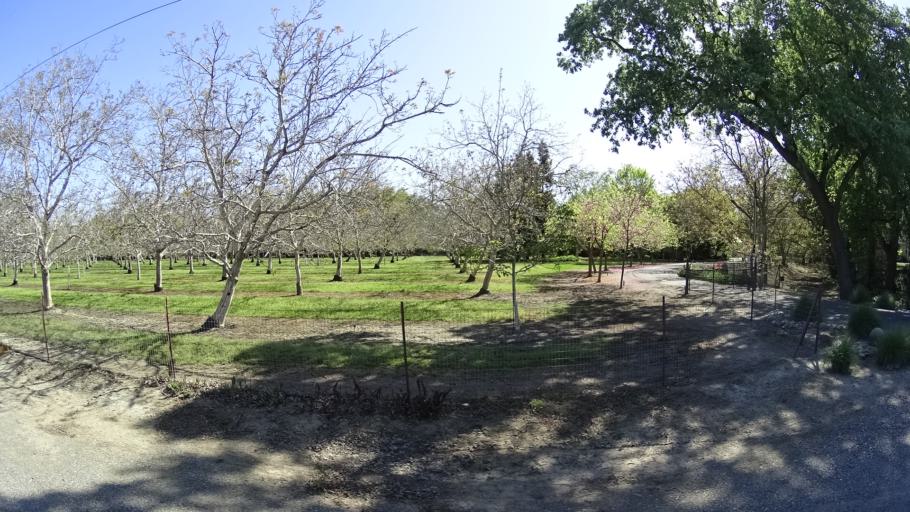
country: US
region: California
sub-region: Glenn County
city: Hamilton City
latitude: 39.7254
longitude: -122.0133
